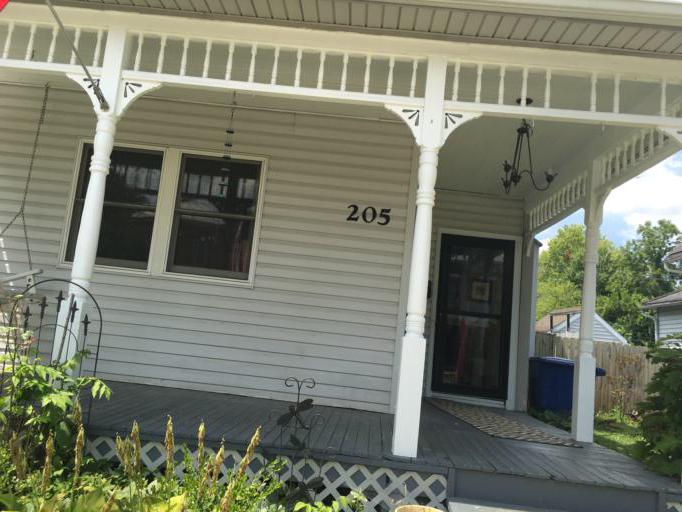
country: US
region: Ohio
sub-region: Delaware County
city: Delaware
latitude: 40.3048
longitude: -83.0656
